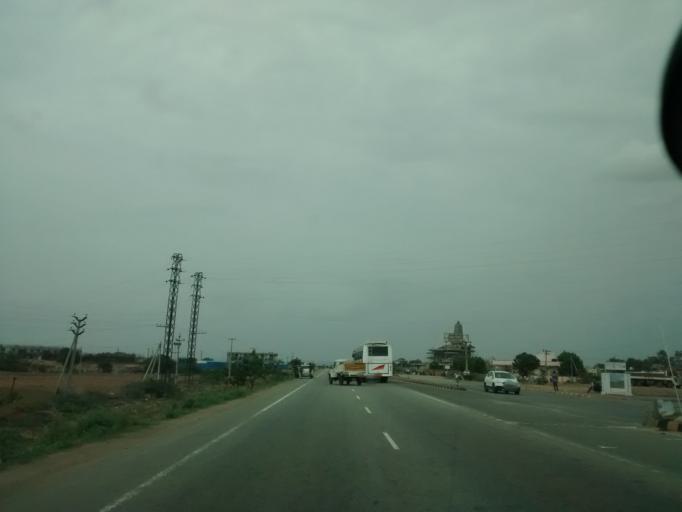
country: IN
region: Andhra Pradesh
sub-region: Kurnool
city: Dhone
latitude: 15.4127
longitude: 77.8763
